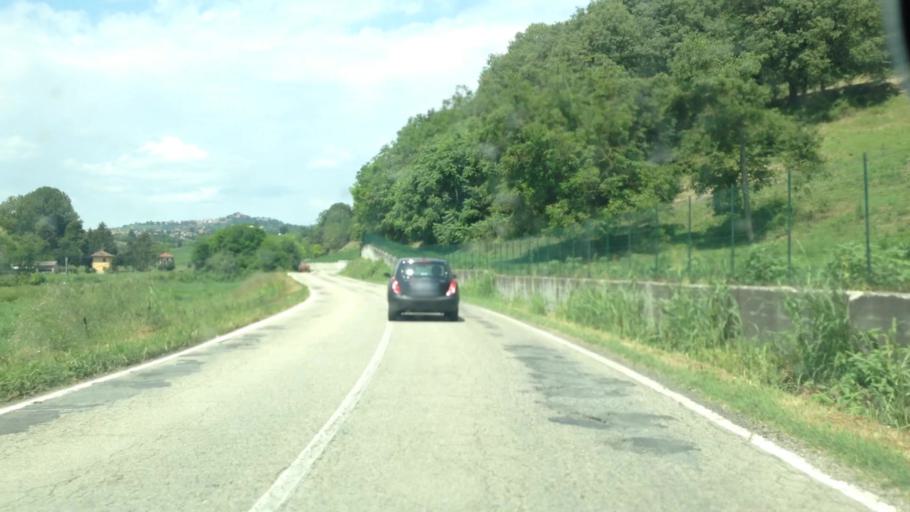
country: IT
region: Piedmont
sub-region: Provincia di Asti
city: Montiglio
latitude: 45.0747
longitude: 8.1007
